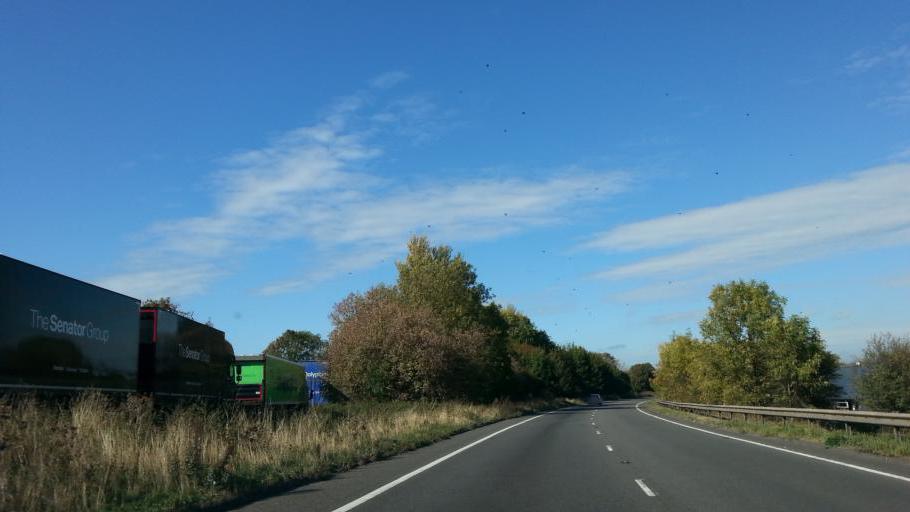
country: GB
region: England
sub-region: District of Rutland
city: Clipsham
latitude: 52.7075
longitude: -0.5895
